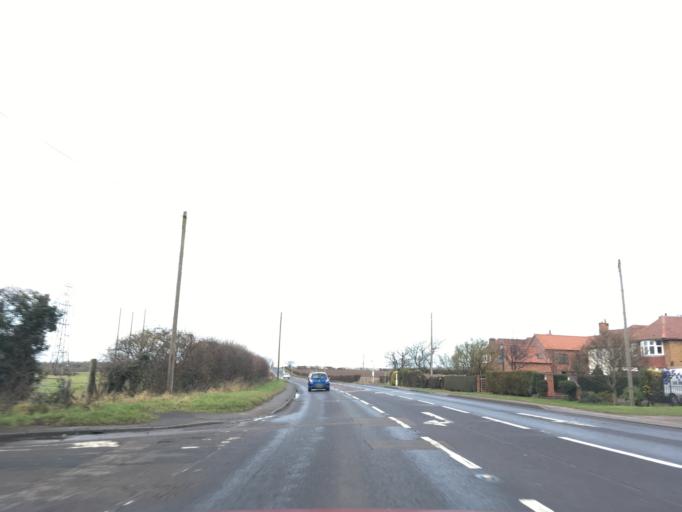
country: GB
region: England
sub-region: Nottinghamshire
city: Ruddington
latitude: 52.8772
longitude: -1.1318
